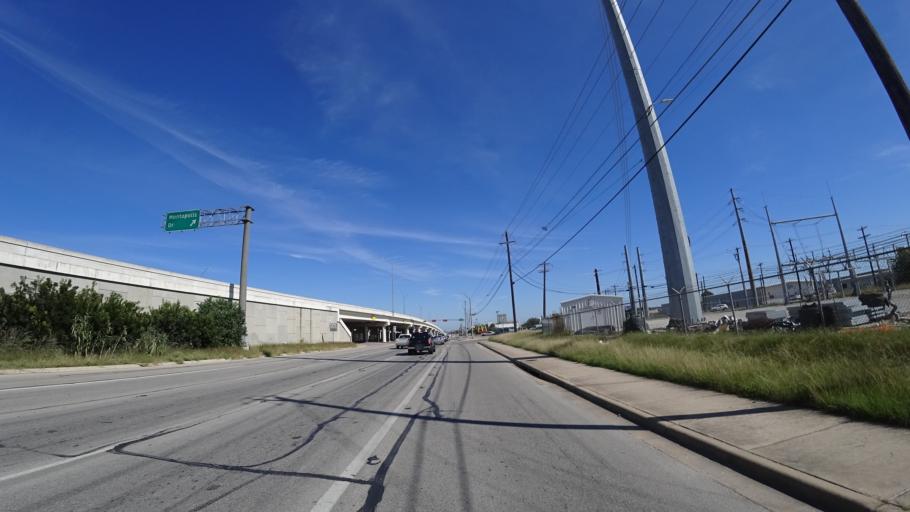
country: US
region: Texas
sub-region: Travis County
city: Austin
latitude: 30.2150
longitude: -97.7364
